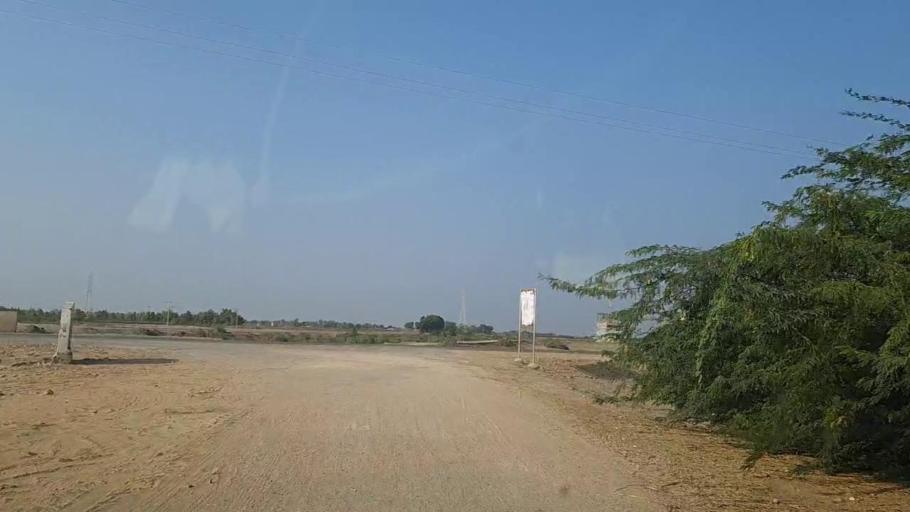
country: PK
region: Sindh
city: Mirpur Sakro
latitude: 24.5602
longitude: 67.6711
